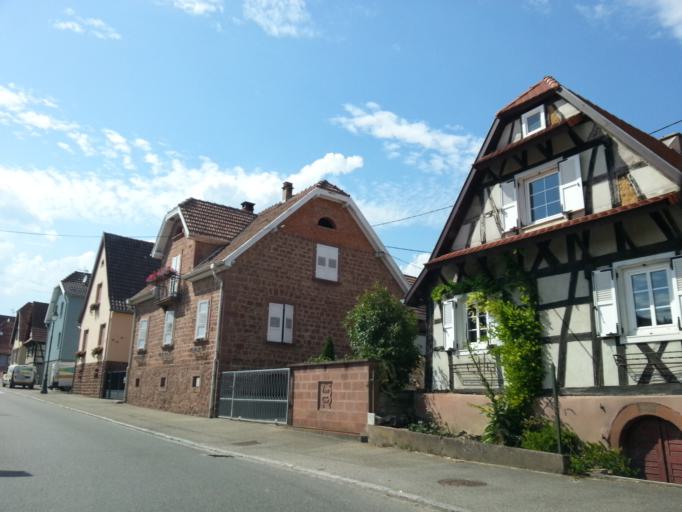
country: FR
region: Alsace
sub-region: Departement du Bas-Rhin
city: Goersdorf
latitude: 48.9456
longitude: 7.7211
